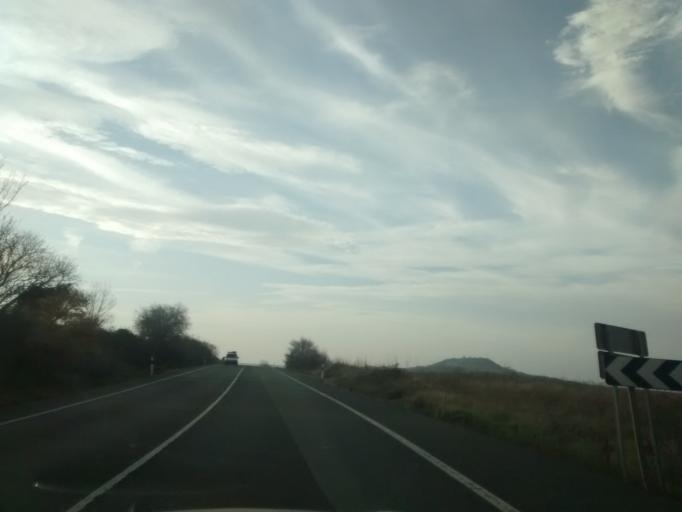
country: ES
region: La Rioja
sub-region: Provincia de La Rioja
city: Gimileo
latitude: 42.5491
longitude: -2.8090
